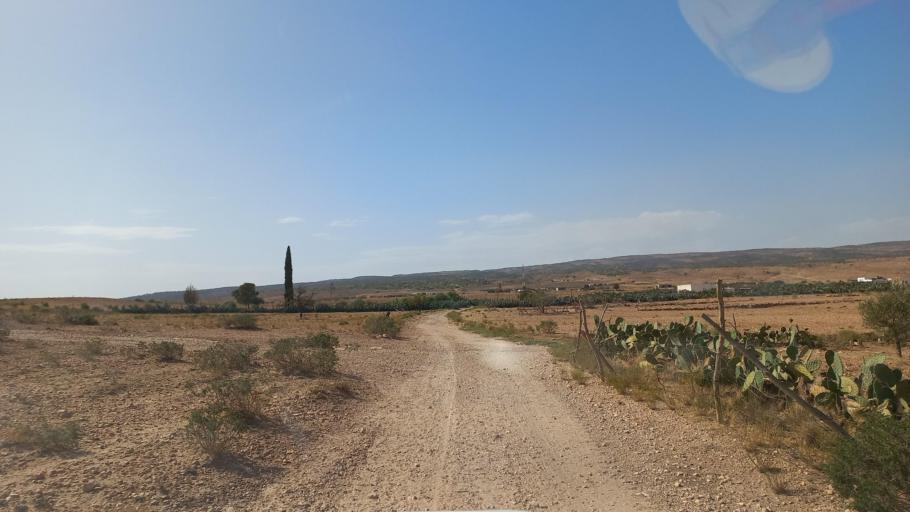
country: TN
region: Al Qasrayn
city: Kasserine
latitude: 35.2812
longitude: 8.9358
